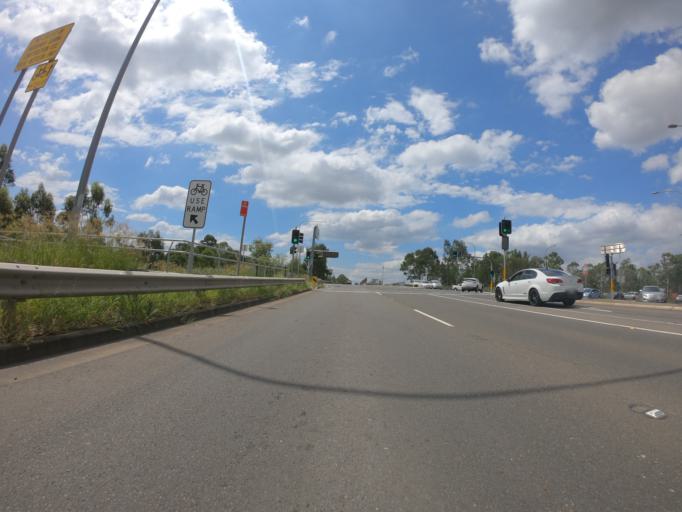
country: AU
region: New South Wales
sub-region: Blacktown
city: Mount Druitt
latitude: -33.7855
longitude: 150.7706
